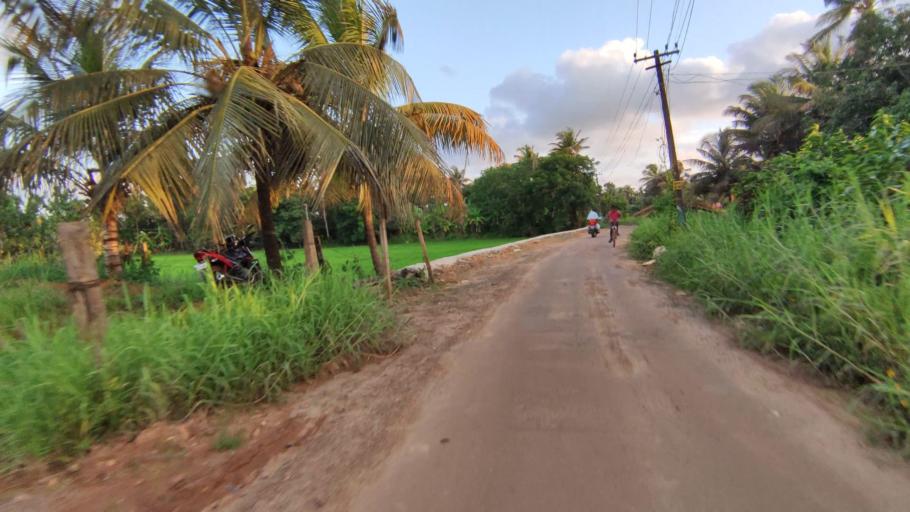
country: IN
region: Kerala
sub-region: Kottayam
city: Kottayam
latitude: 9.5855
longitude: 76.4480
